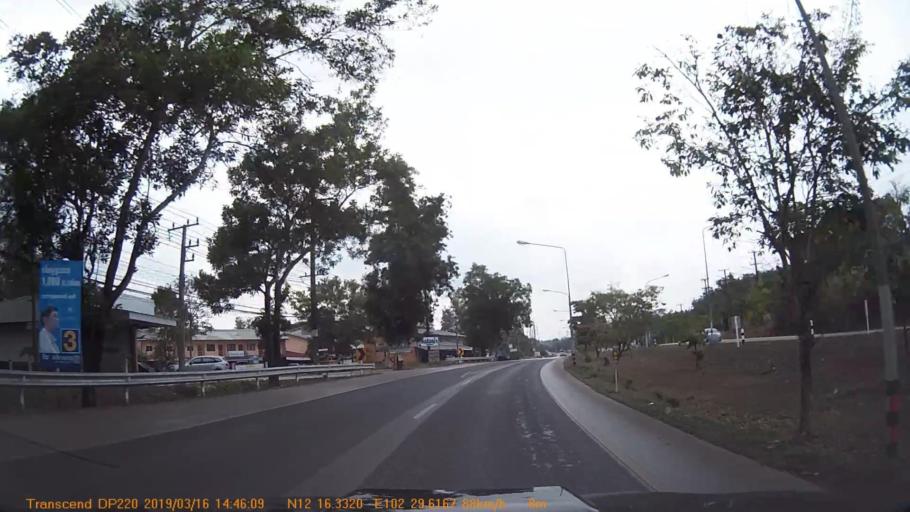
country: TH
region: Trat
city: Trat
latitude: 12.2723
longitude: 102.4935
